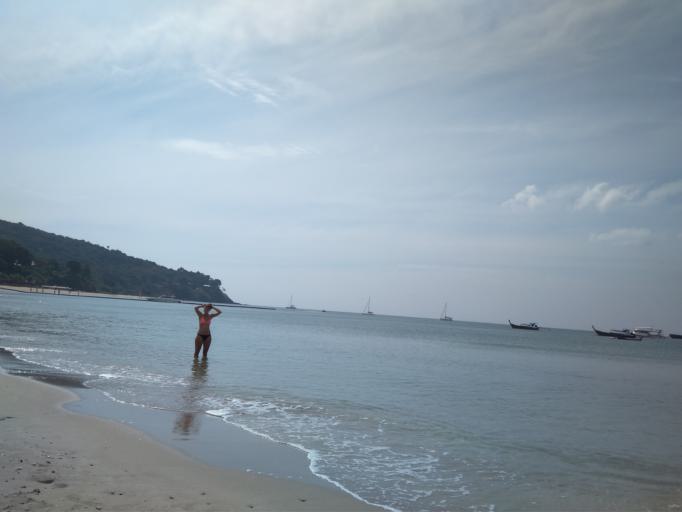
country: TH
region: Krabi
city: Ko Lanta
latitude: 7.4979
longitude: 99.0726
